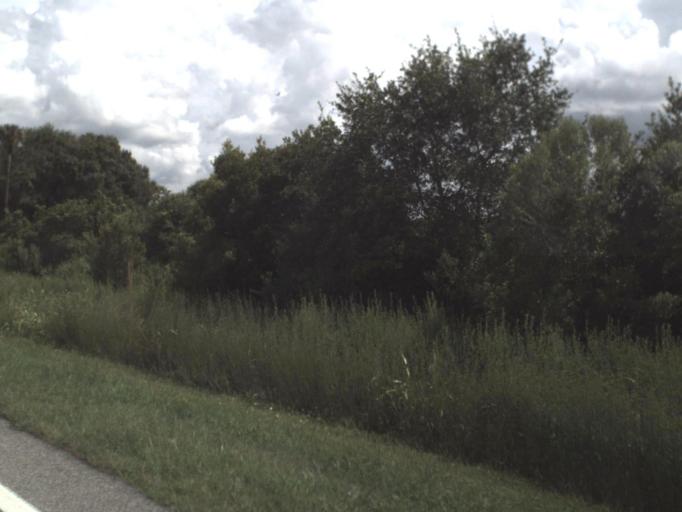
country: US
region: Florida
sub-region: Sarasota County
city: Warm Mineral Springs
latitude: 27.2172
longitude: -82.2749
